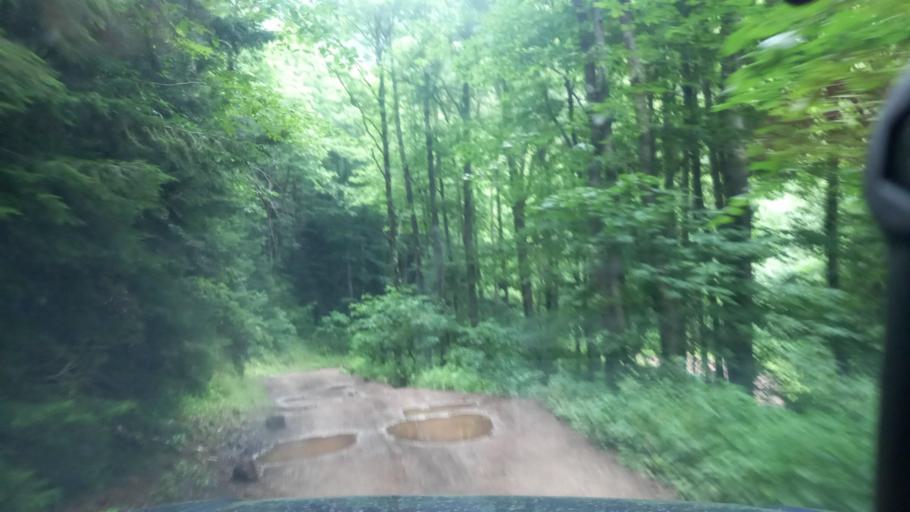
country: RU
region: Karachayevo-Cherkesiya
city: Kurdzhinovo
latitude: 43.8148
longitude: 40.8798
